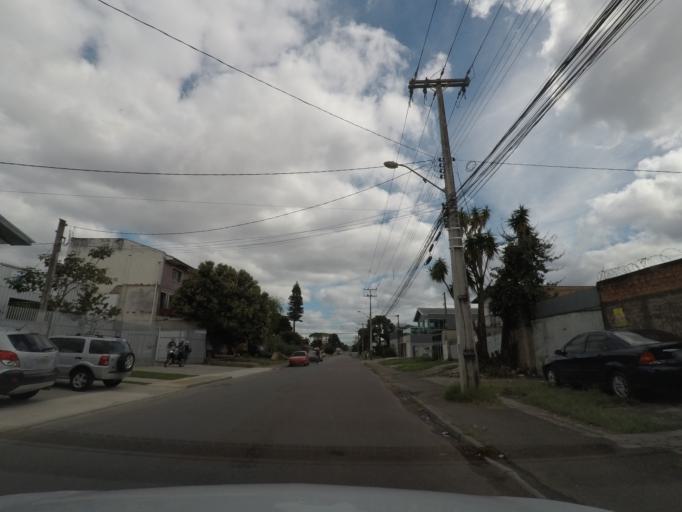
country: BR
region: Parana
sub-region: Sao Jose Dos Pinhais
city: Sao Jose dos Pinhais
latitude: -25.4853
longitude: -49.2364
